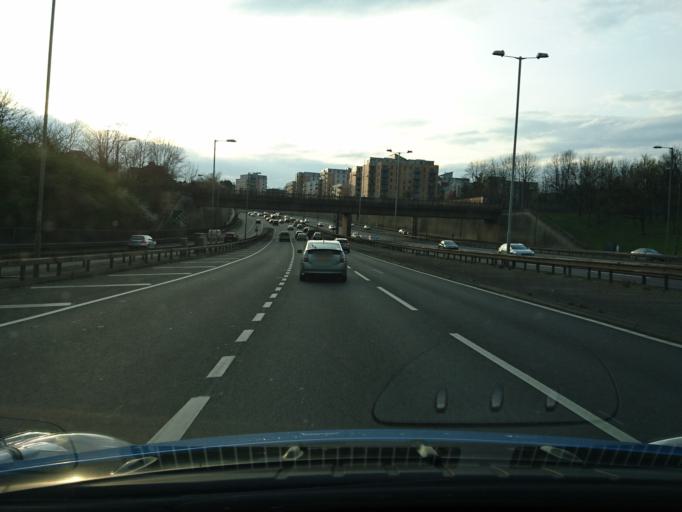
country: GB
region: England
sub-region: Greater London
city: Woodford Green
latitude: 51.5956
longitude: 0.0301
